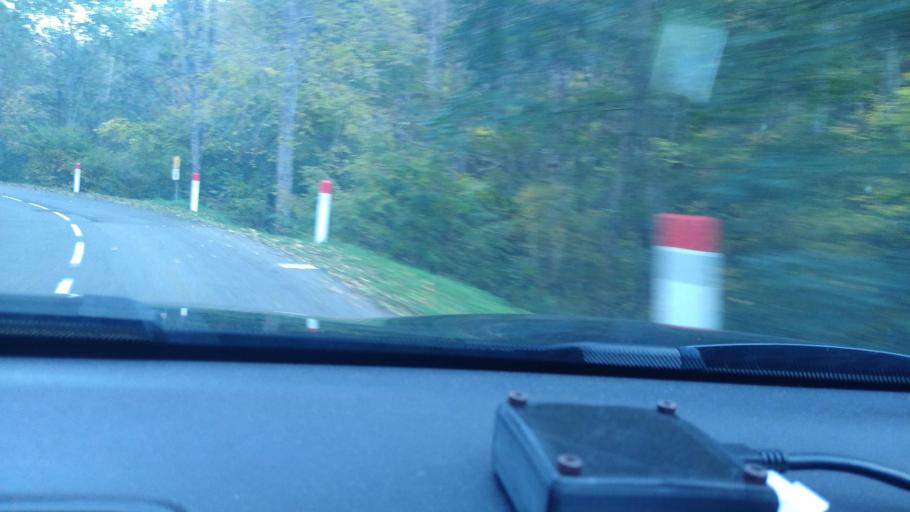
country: FR
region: Languedoc-Roussillon
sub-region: Departement de l'Aude
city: Quillan
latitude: 42.7278
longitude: 2.1076
